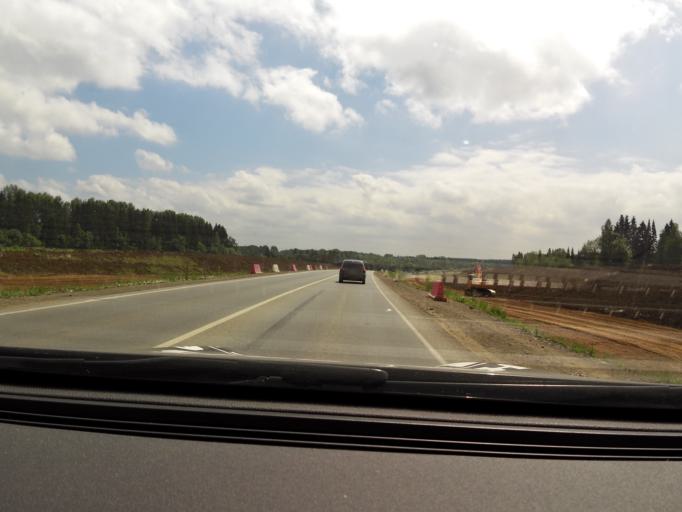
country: RU
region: Perm
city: Bershet'
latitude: 57.6799
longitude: 56.4292
